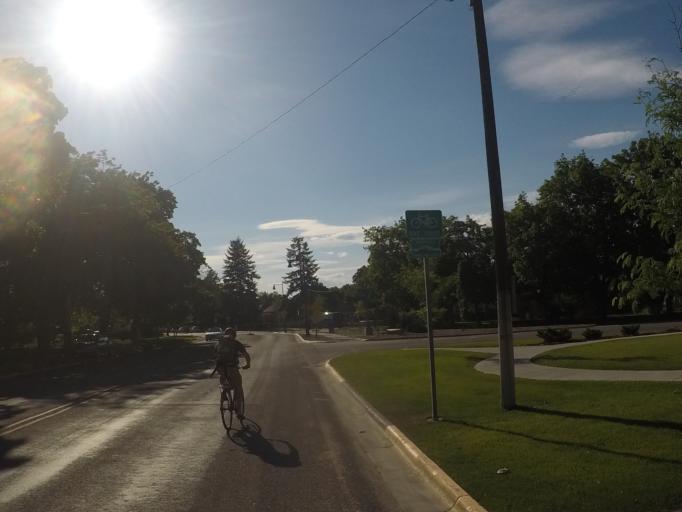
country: US
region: Montana
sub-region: Missoula County
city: Missoula
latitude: 46.8777
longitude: -114.0049
